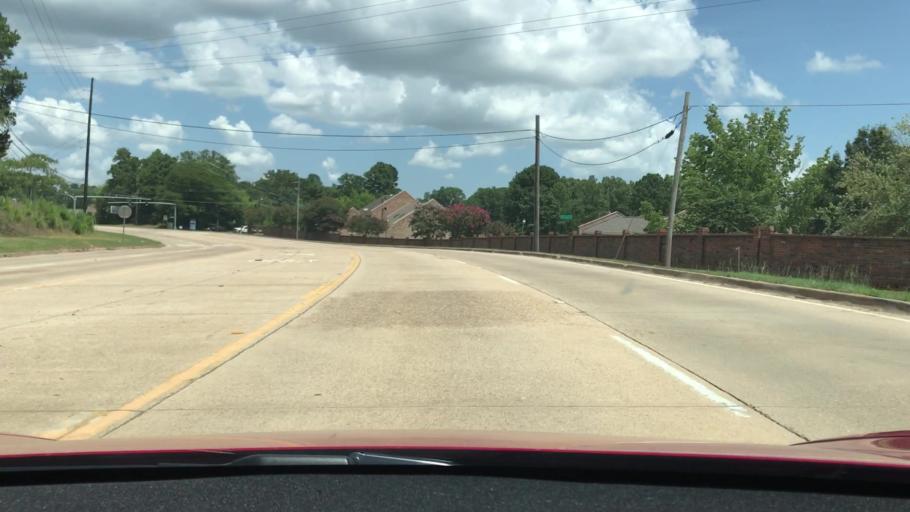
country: US
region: Louisiana
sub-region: Bossier Parish
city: Bossier City
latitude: 32.4199
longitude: -93.7360
